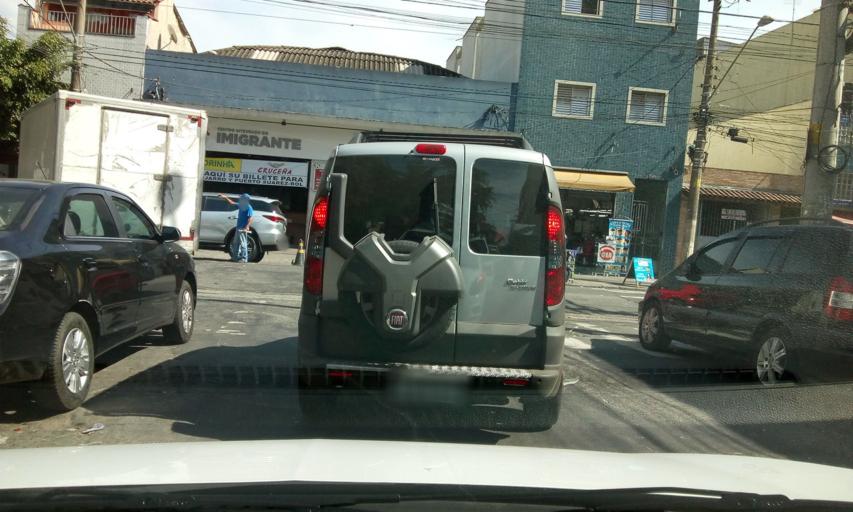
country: BR
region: Sao Paulo
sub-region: Sao Paulo
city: Sao Paulo
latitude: -23.5414
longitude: -46.6097
